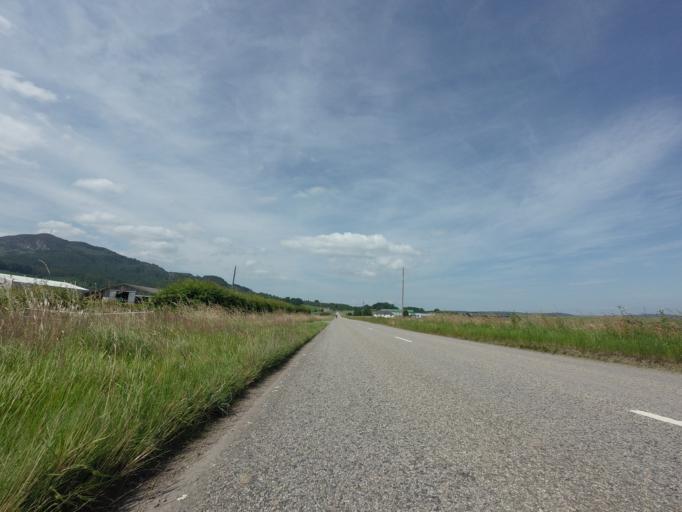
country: GB
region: Scotland
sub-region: Highland
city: Tain
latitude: 57.8446
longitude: -4.1982
